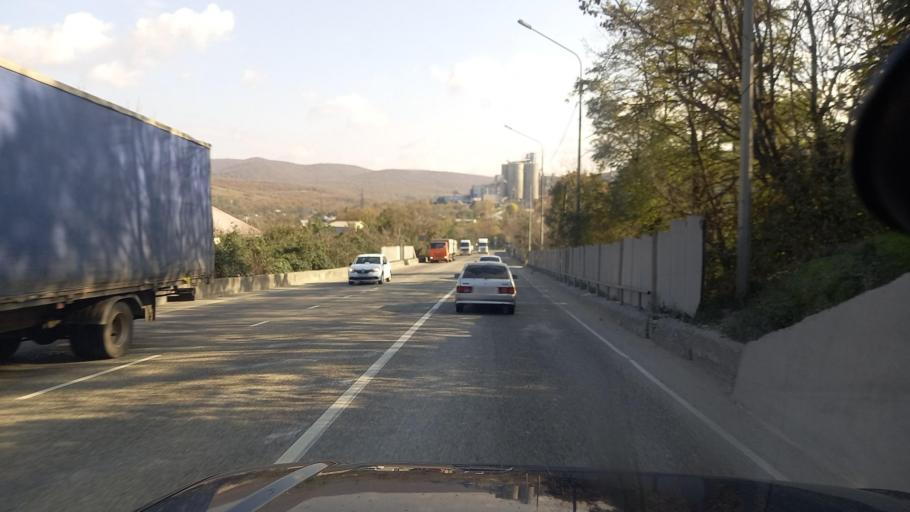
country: RU
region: Krasnodarskiy
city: Verkhnebakanskiy
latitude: 44.8372
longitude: 37.6661
